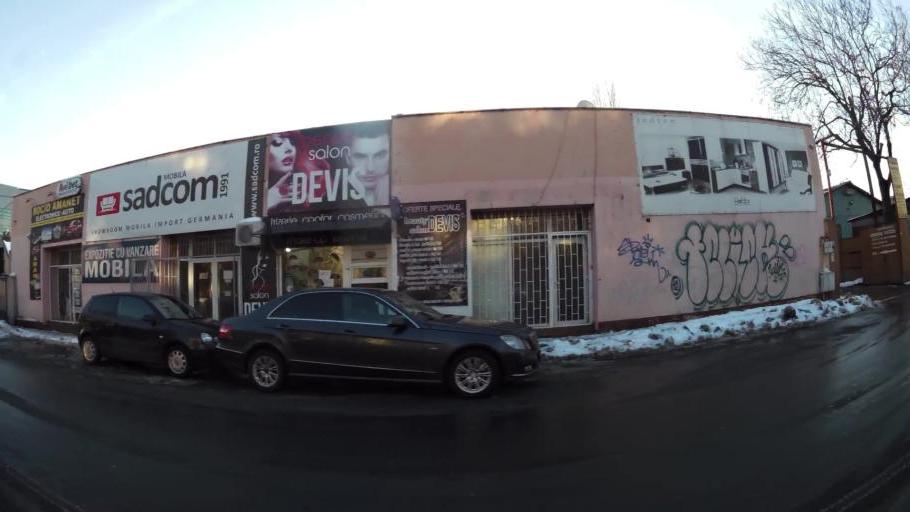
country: RO
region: Ilfov
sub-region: Comuna Fundeni-Dobroesti
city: Fundeni
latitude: 44.4504
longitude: 26.1476
